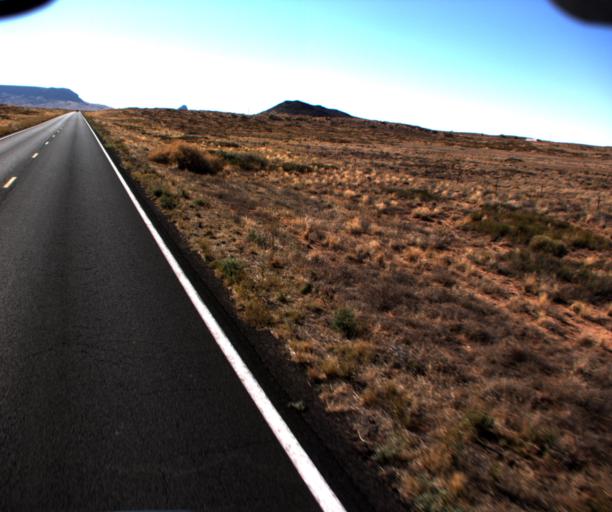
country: US
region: Arizona
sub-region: Navajo County
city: Dilkon
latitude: 35.4780
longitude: -110.4264
